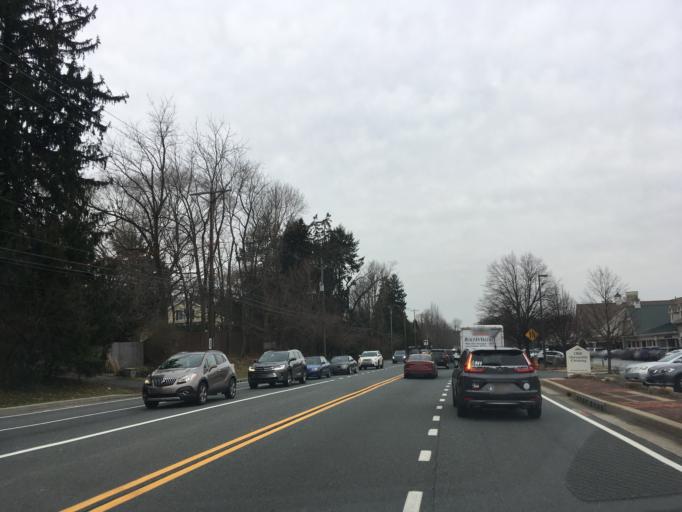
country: US
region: Delaware
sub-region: New Castle County
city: Greenville
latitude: 39.7791
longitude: -75.5985
